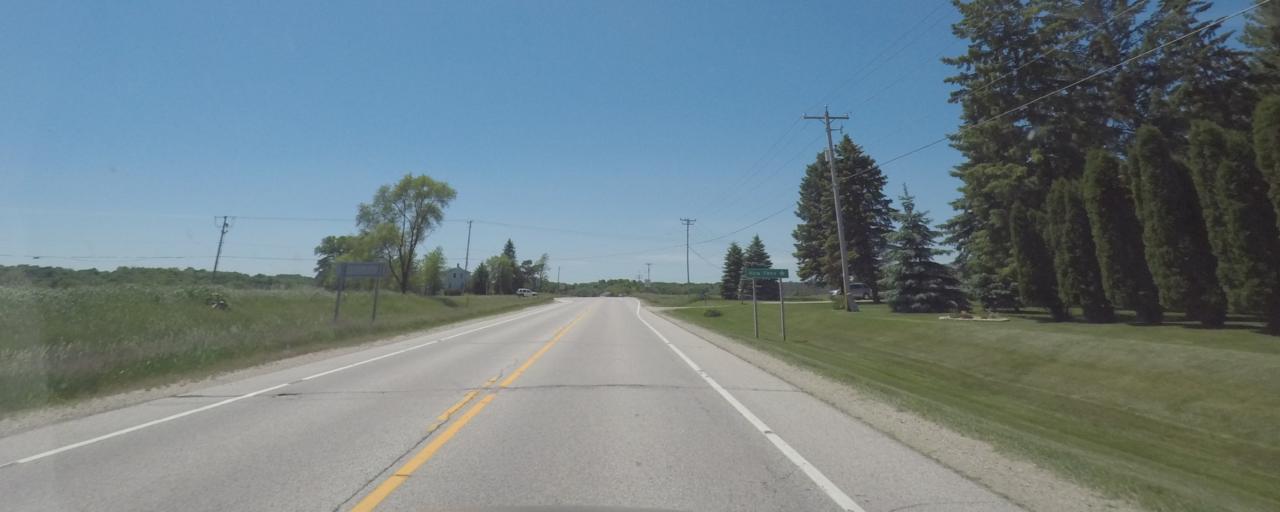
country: US
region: Wisconsin
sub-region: Ozaukee County
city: Kohler
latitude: 43.5581
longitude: -88.0738
